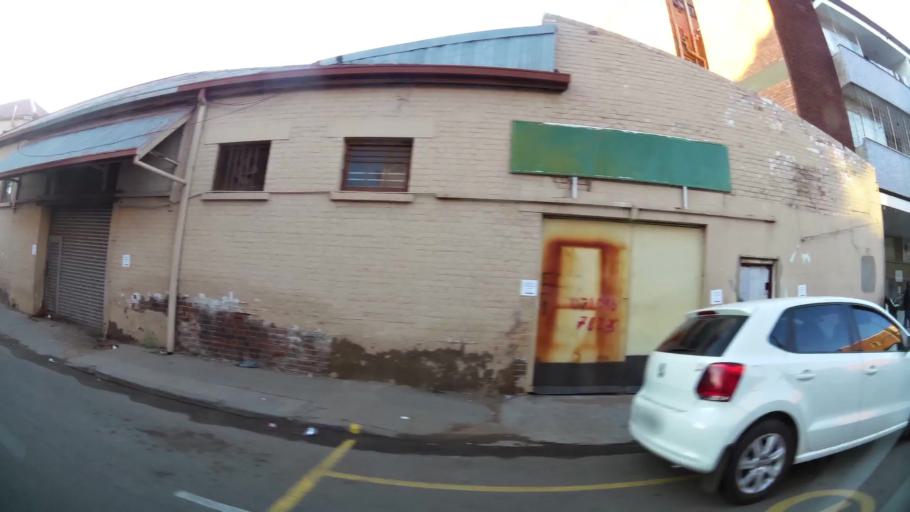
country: ZA
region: Northern Cape
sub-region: Frances Baard District Municipality
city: Kimberley
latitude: -28.7389
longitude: 24.7645
